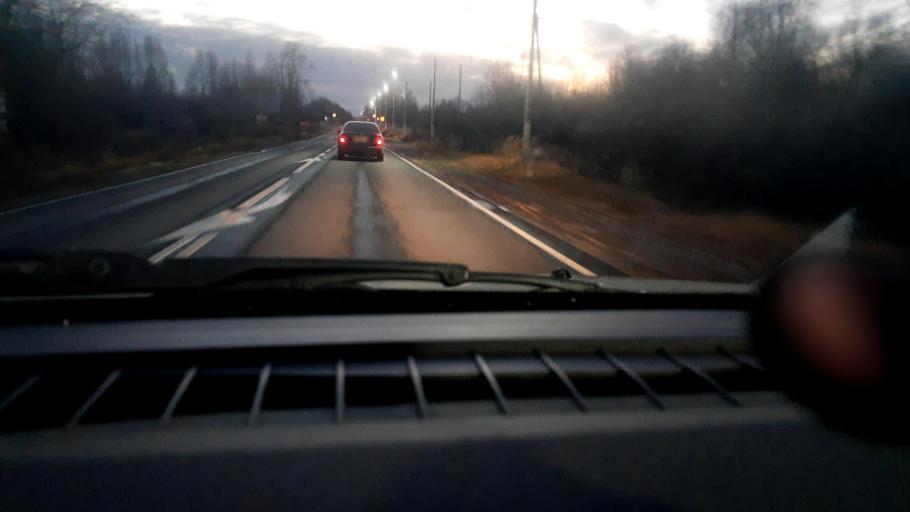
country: RU
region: Nizjnij Novgorod
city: Sukhobezvodnoye
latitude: 56.8704
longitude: 44.9383
